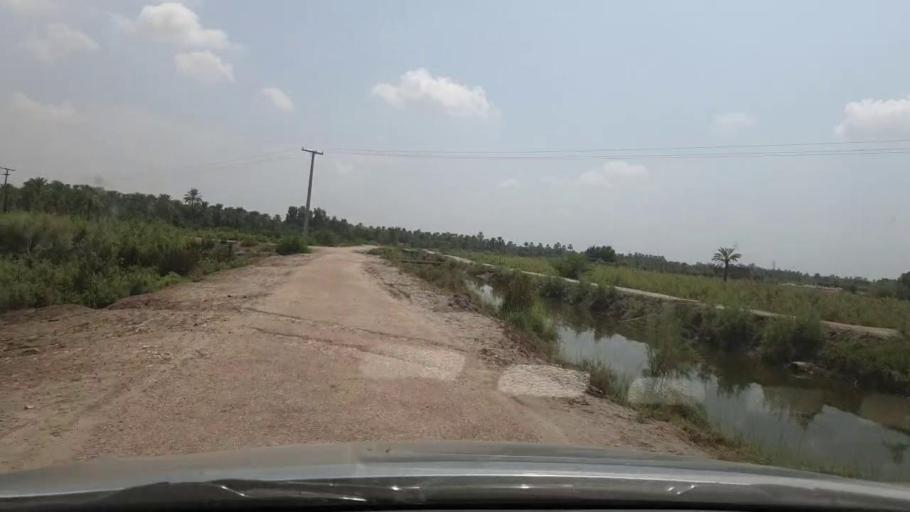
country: PK
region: Sindh
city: Kot Diji
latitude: 27.3769
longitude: 68.7105
